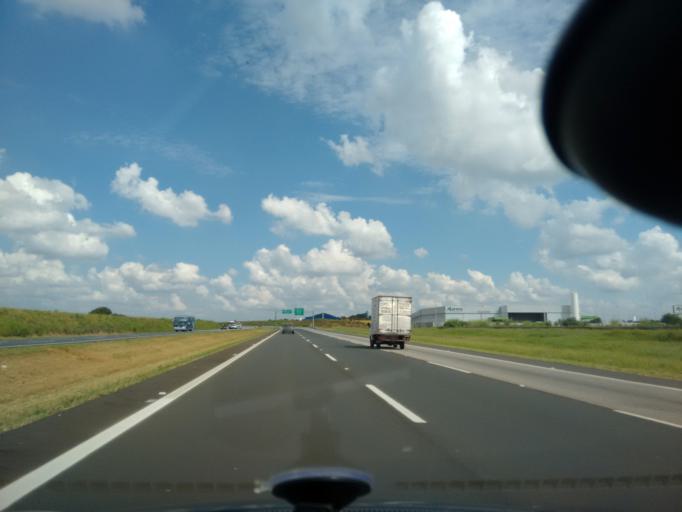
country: BR
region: Sao Paulo
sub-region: Hortolandia
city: Hortolandia
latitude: -22.8895
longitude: -47.2289
